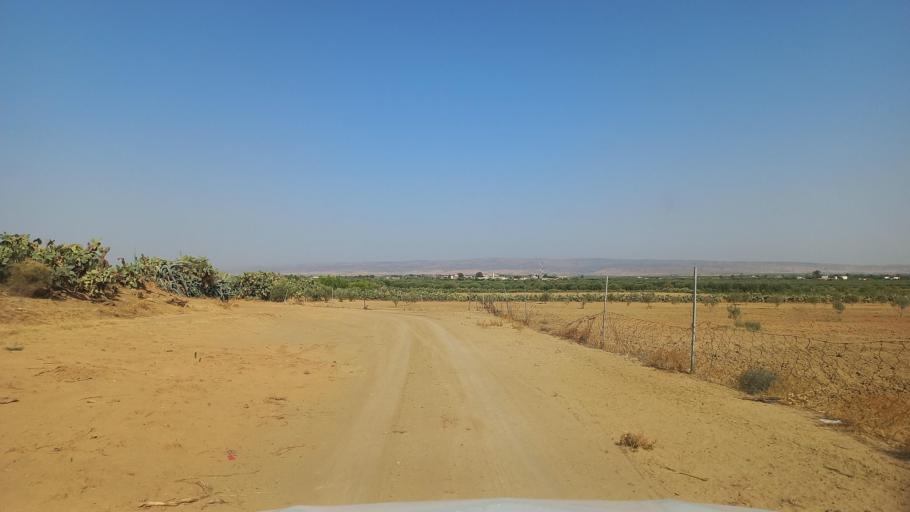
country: TN
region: Al Qasrayn
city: Kasserine
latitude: 35.2437
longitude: 9.0405
